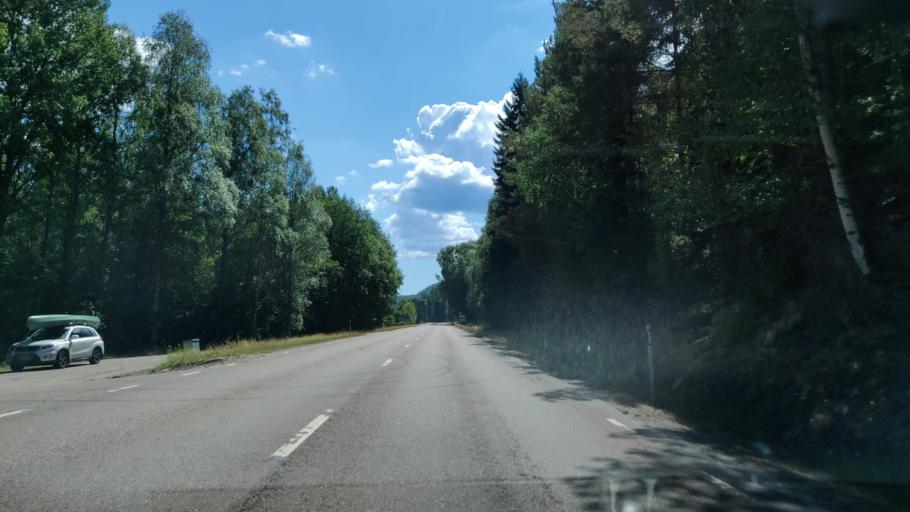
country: SE
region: Vaermland
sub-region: Hagfors Kommun
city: Ekshaerad
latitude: 60.1855
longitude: 13.4970
